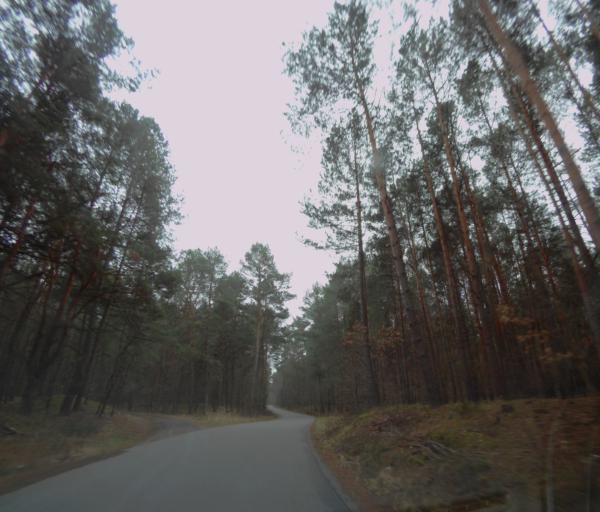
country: PL
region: Subcarpathian Voivodeship
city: Nowa Sarzyna
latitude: 50.3052
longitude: 22.3464
